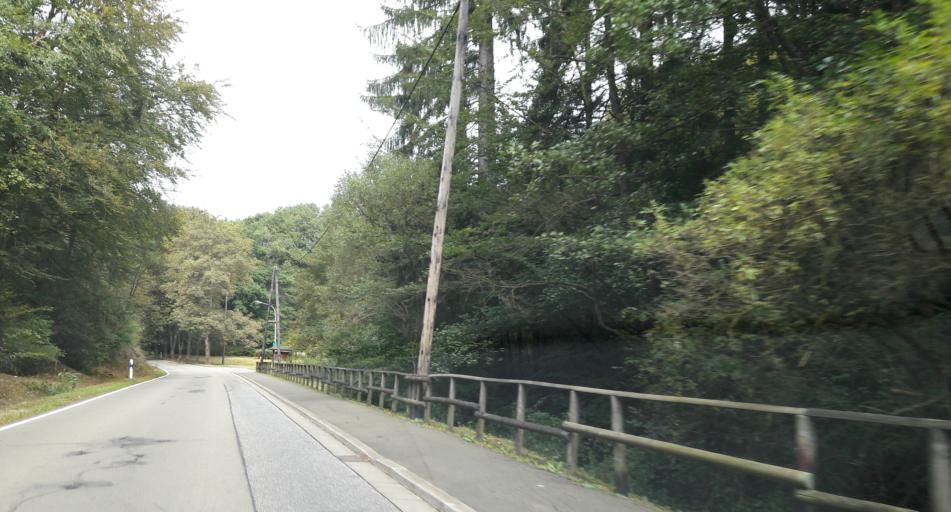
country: DE
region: Rheinland-Pfalz
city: Hahnweiler
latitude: 49.5185
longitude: 7.2111
